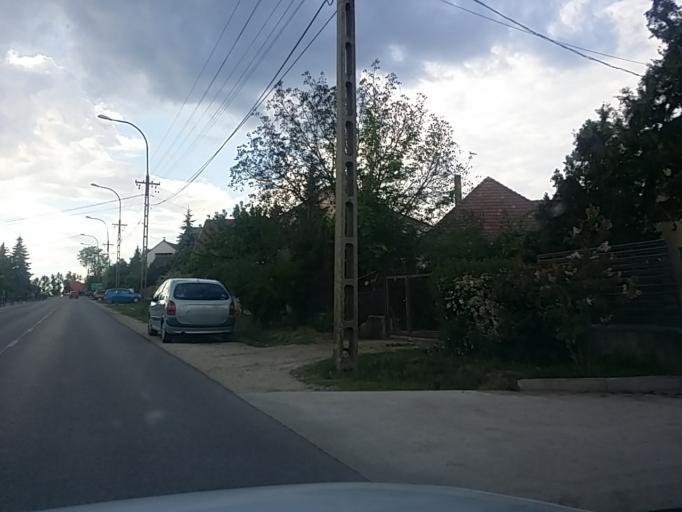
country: HU
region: Pest
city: Veresegyhaz
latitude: 47.6560
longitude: 19.2744
